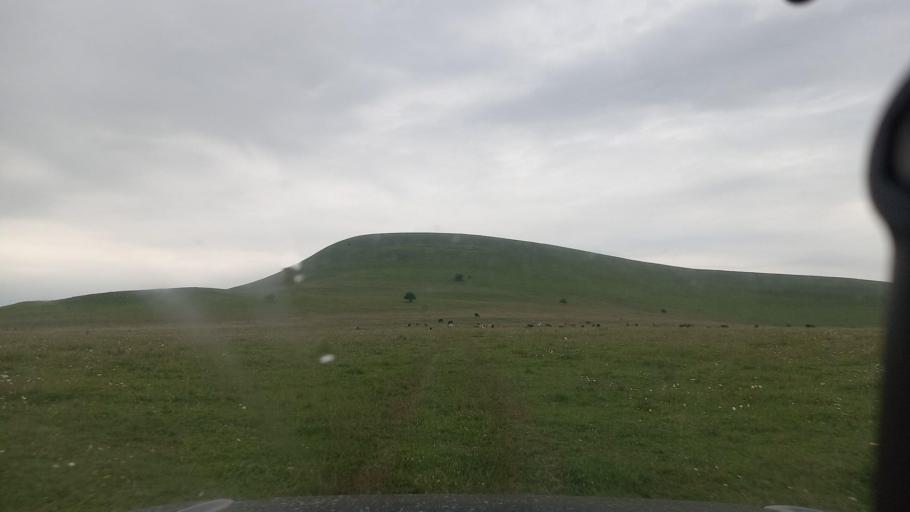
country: RU
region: Karachayevo-Cherkesiya
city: Pregradnaya
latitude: 43.9500
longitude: 41.1617
